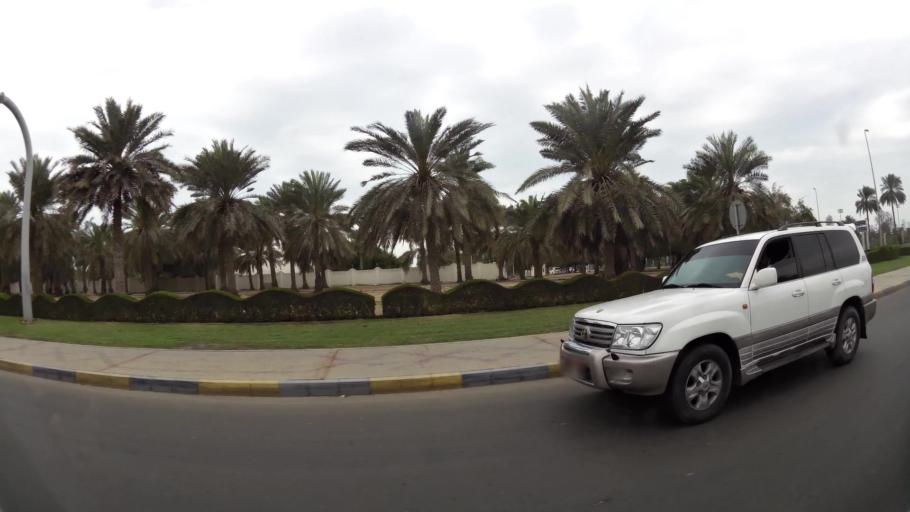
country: AE
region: Abu Dhabi
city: Abu Dhabi
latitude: 24.4368
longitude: 54.3789
